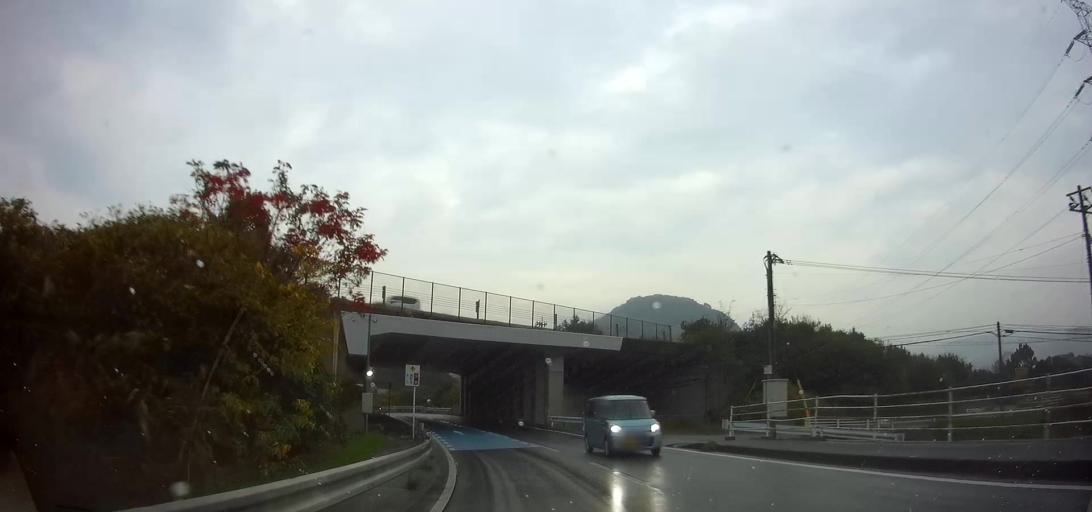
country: JP
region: Nagasaki
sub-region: Isahaya-shi
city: Isahaya
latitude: 32.8492
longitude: 130.0102
